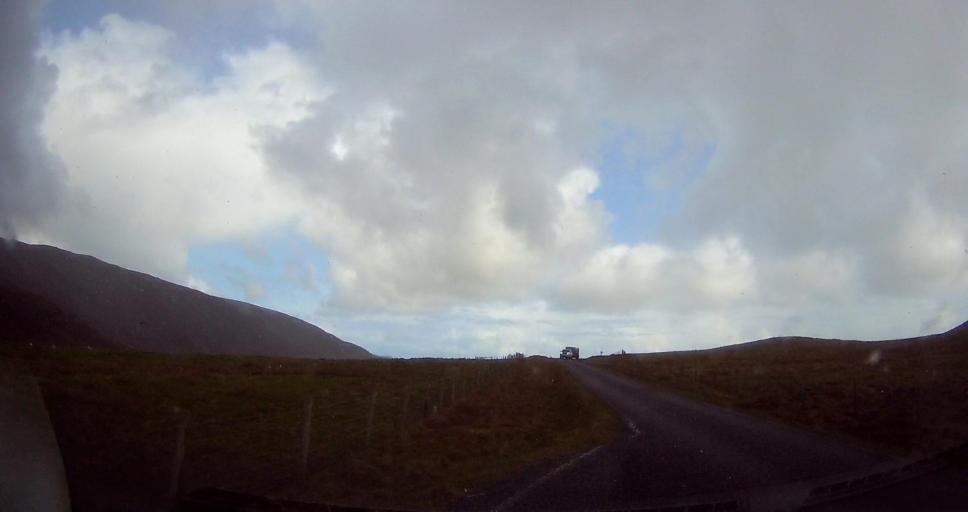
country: GB
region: Scotland
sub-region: Shetland Islands
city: Lerwick
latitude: 60.5563
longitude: -1.3397
